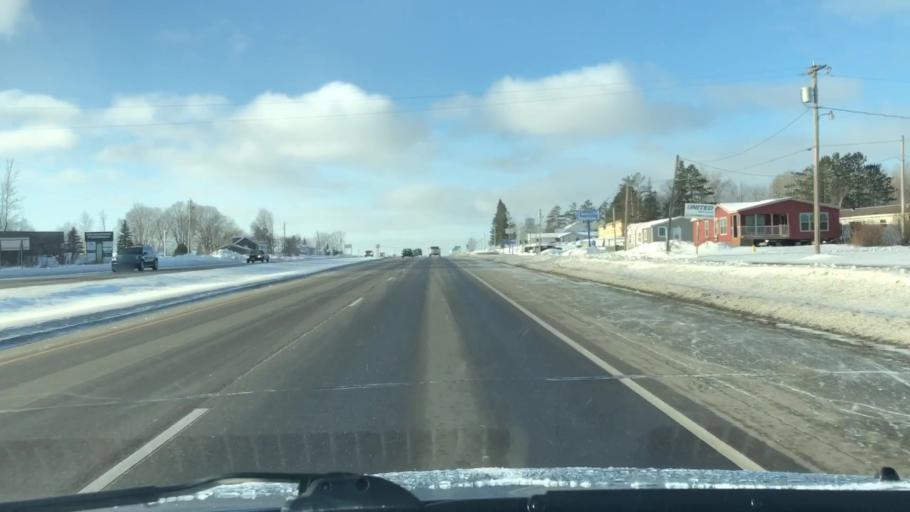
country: US
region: Minnesota
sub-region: Saint Louis County
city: Hermantown
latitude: 46.8238
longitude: -92.1893
